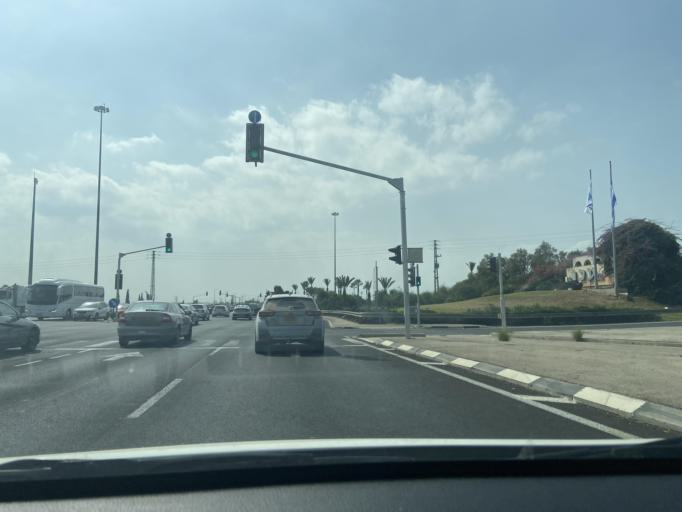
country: IL
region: Northern District
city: `Akko
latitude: 32.9206
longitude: 35.0970
